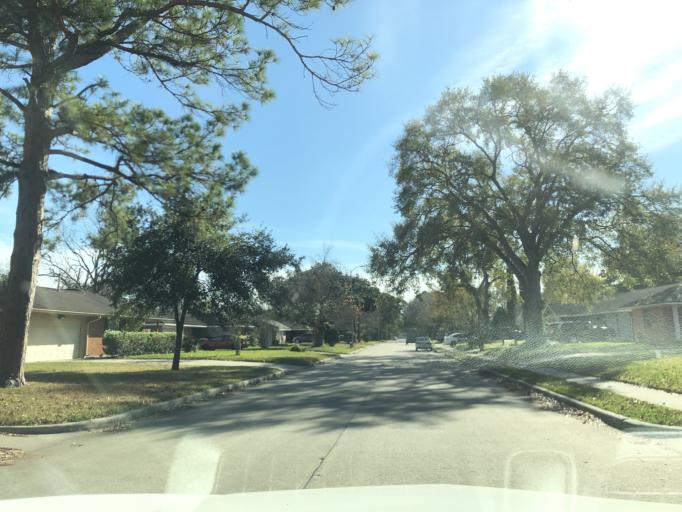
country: US
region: Texas
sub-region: Harris County
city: Bellaire
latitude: 29.6804
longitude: -95.5109
